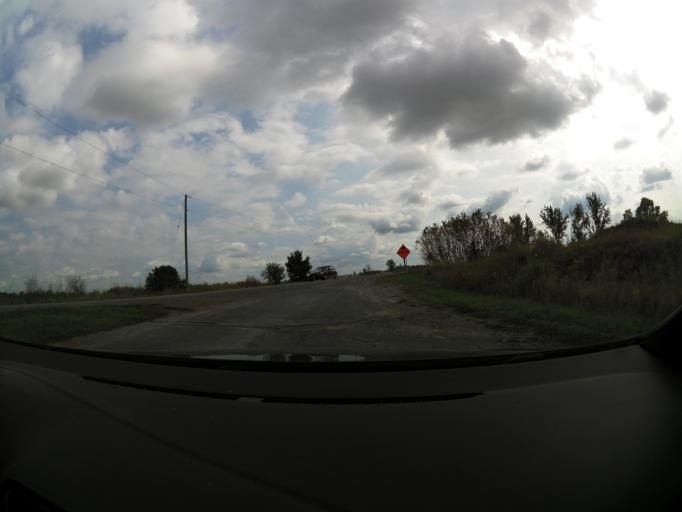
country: CA
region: Ontario
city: Arnprior
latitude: 45.3877
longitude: -76.2534
